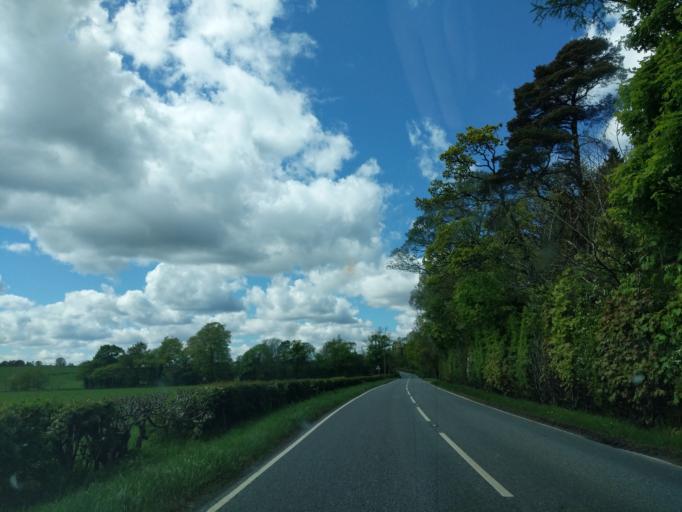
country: GB
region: Scotland
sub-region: Stirling
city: Doune
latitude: 56.1633
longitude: -4.0761
